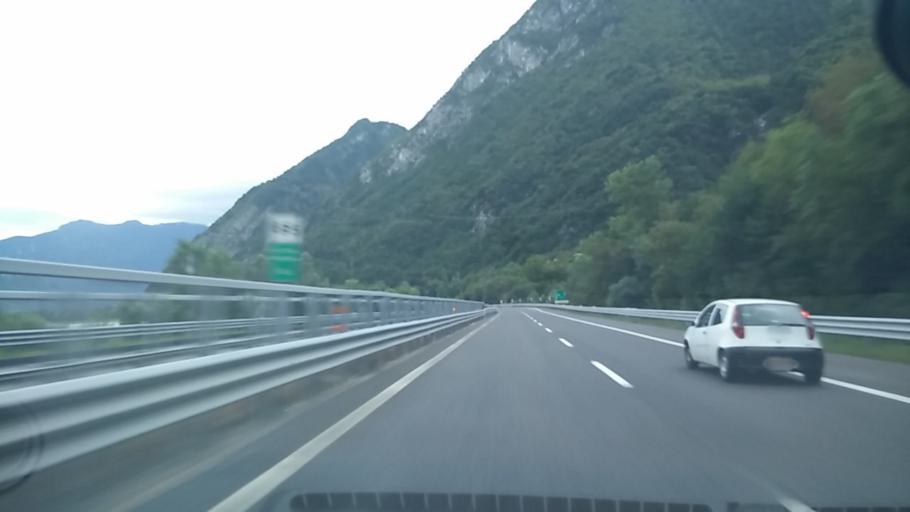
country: IT
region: Friuli Venezia Giulia
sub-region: Provincia di Udine
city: Amaro
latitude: 46.3909
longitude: 13.1372
